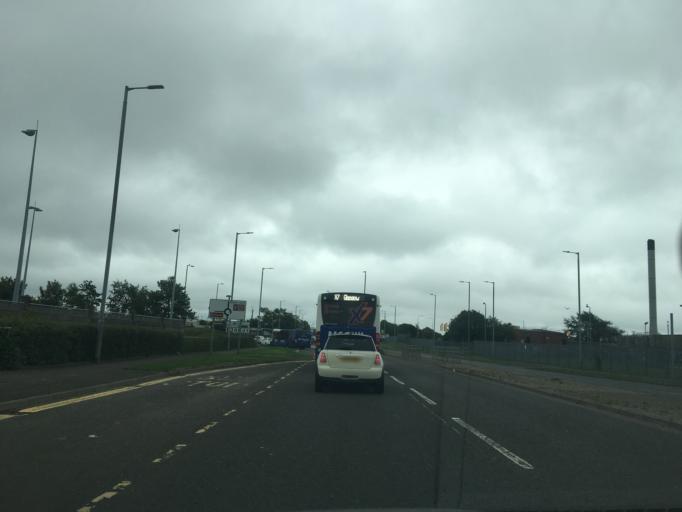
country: GB
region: Scotland
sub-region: Renfrewshire
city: Renfrew
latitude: 55.8731
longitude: -4.3642
